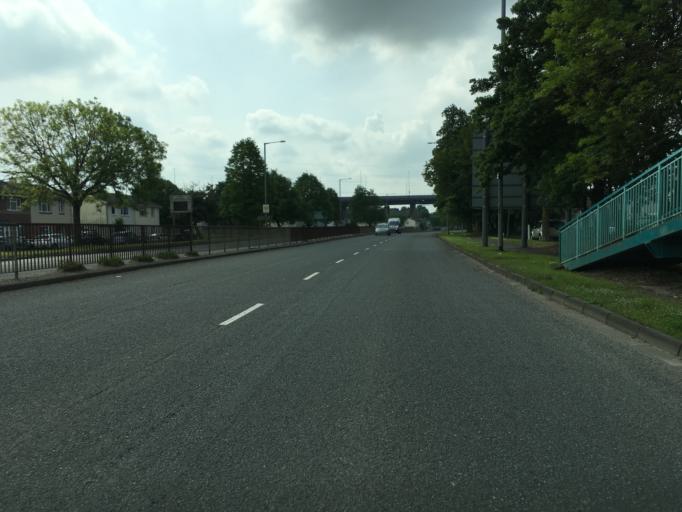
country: GB
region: England
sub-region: North Somerset
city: Easton-in-Gordano
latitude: 51.4962
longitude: -2.6898
